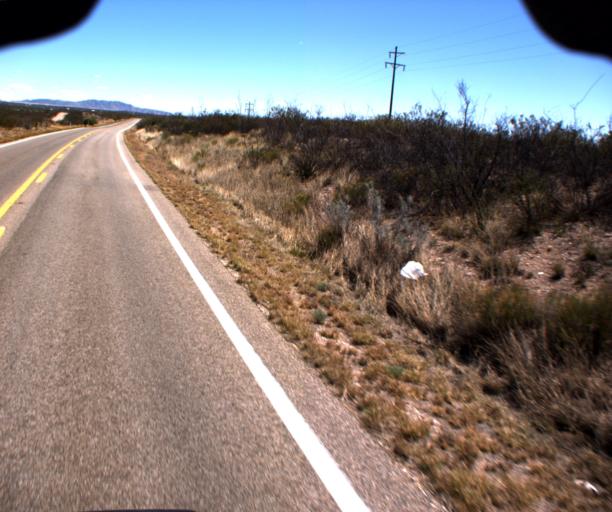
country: US
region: Arizona
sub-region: Cochise County
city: Tombstone
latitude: 31.7482
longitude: -110.1110
